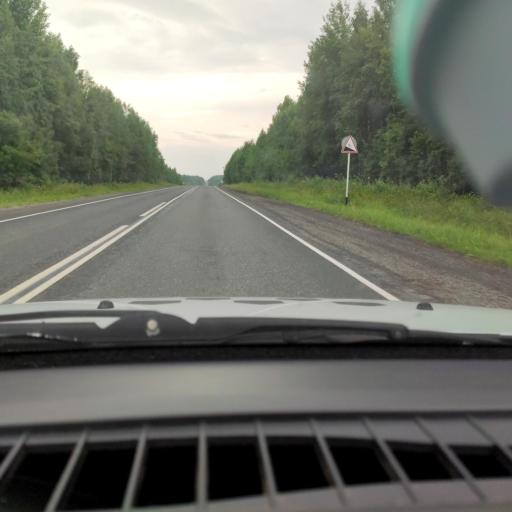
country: RU
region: Perm
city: Berezniki
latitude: 58.9482
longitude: 56.7256
